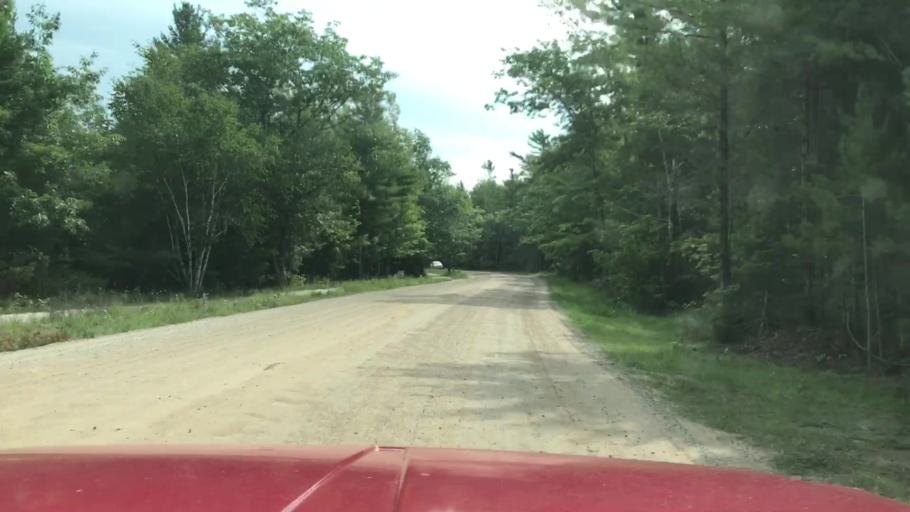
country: US
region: Michigan
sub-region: Charlevoix County
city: Charlevoix
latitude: 45.7471
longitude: -85.5357
